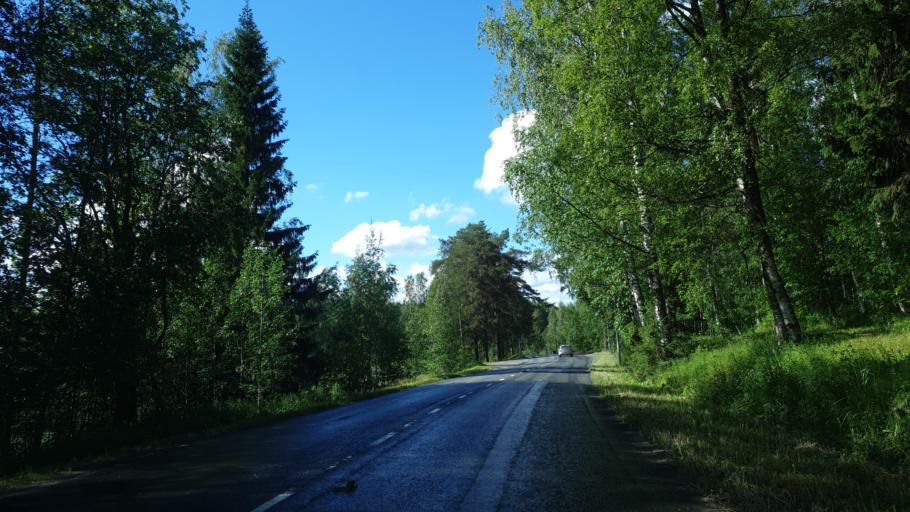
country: FI
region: Northern Savo
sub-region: Kuopio
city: Kuopio
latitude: 62.9167
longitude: 27.6317
